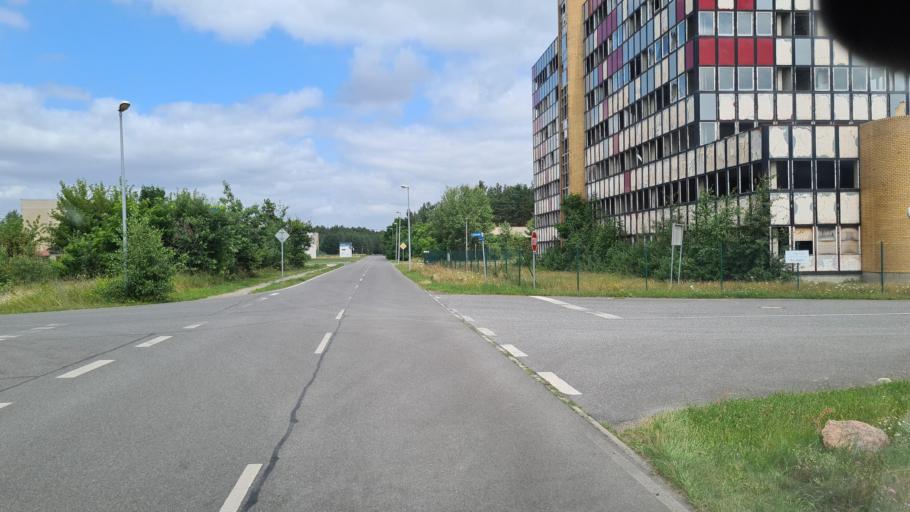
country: DE
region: Brandenburg
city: Grossraschen
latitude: 51.5926
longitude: 14.0197
